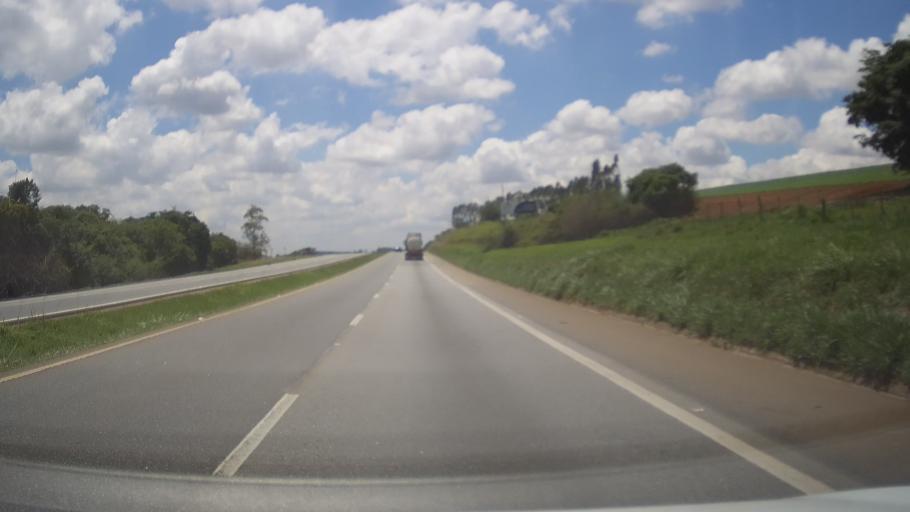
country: BR
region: Minas Gerais
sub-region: Campanha
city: Campanha
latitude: -21.8006
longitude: -45.4679
